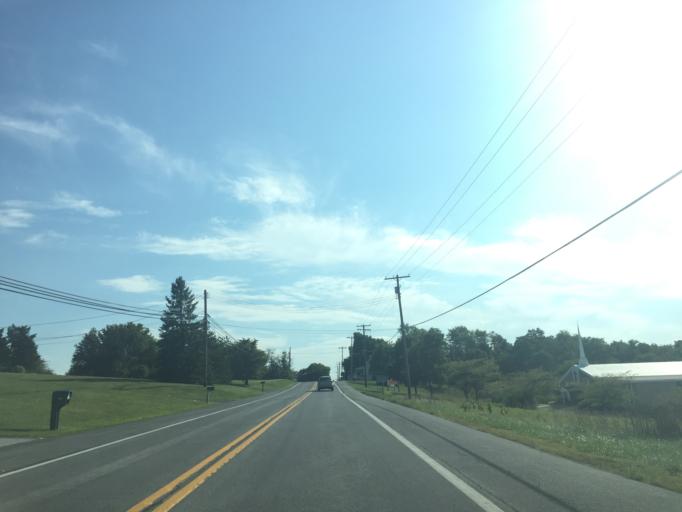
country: US
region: Maryland
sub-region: Carroll County
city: Mount Airy
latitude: 39.3906
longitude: -77.1425
